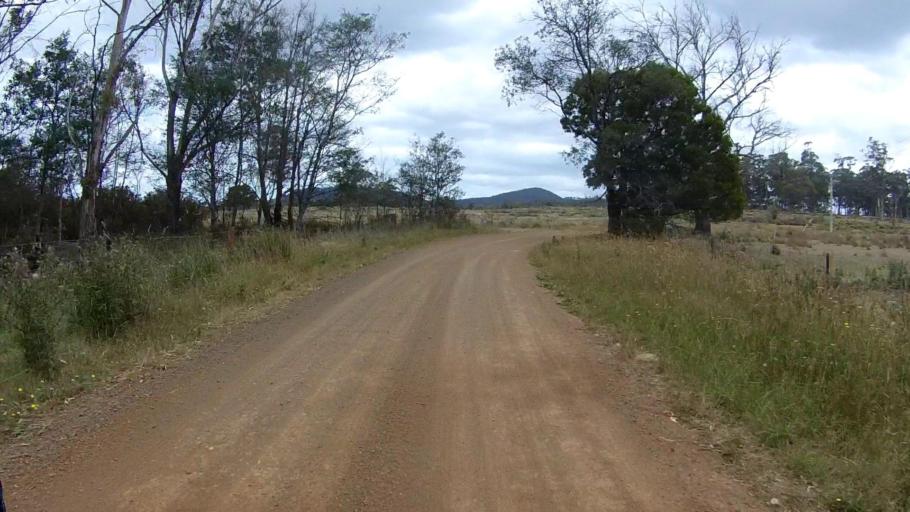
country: AU
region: Tasmania
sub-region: Sorell
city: Sorell
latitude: -42.6412
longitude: 147.9070
